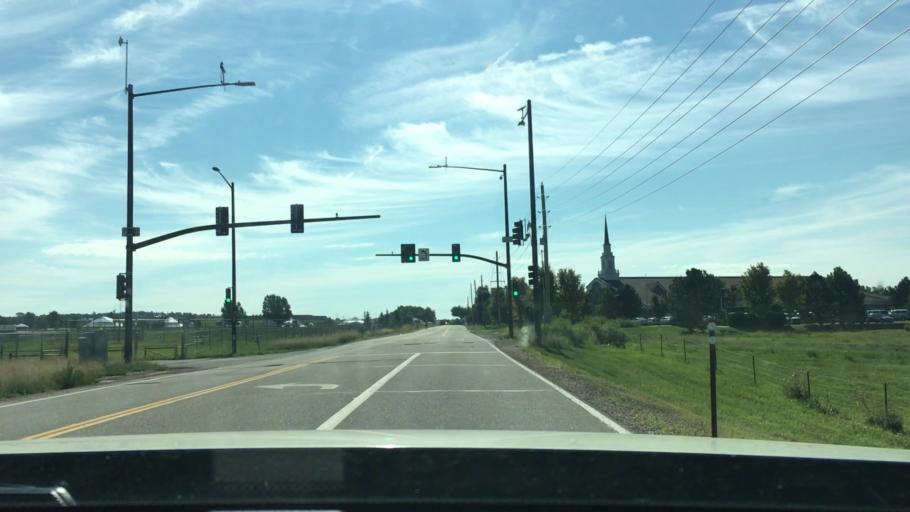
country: US
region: Colorado
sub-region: Douglas County
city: The Pinery
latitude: 39.4335
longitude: -104.7544
